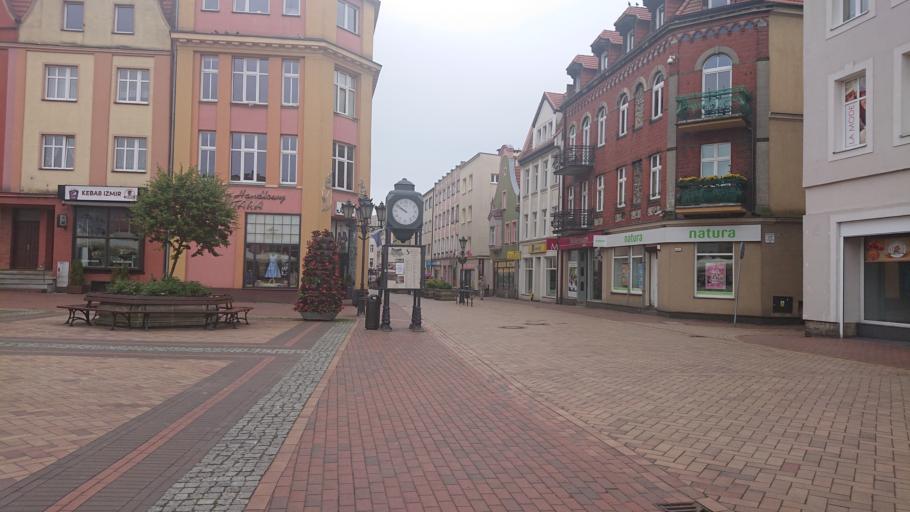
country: PL
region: Pomeranian Voivodeship
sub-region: Powiat chojnicki
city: Chojnice
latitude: 53.6952
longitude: 17.5614
